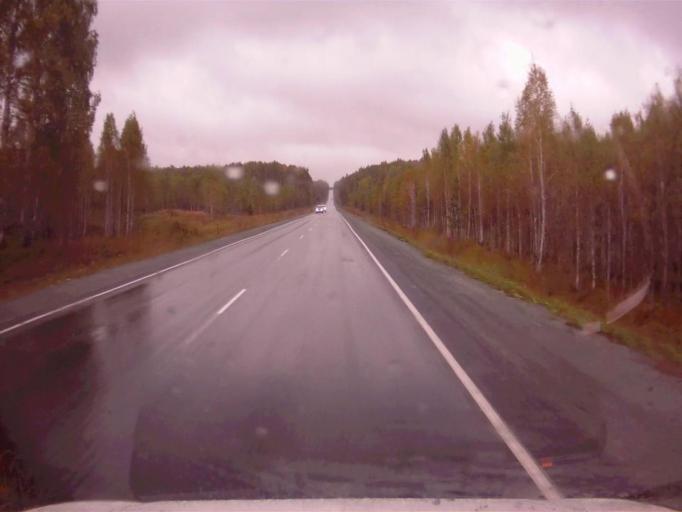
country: RU
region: Chelyabinsk
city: Tayginka
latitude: 55.5146
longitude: 60.6400
